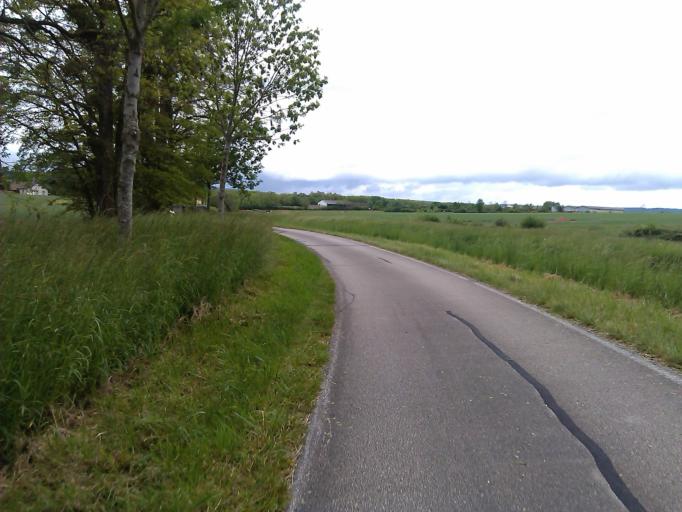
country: FR
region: Bourgogne
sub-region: Departement de Saone-et-Loire
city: Chagny
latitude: 46.8881
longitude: 4.7642
